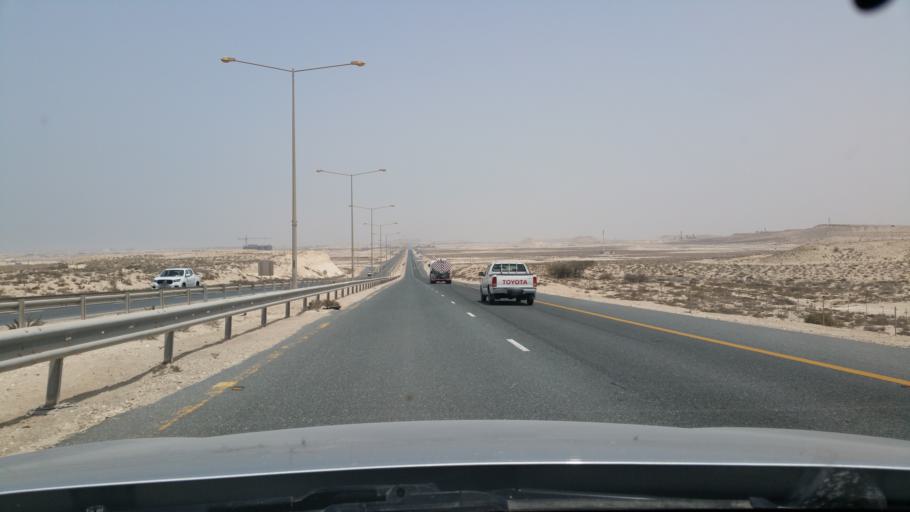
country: QA
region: Baladiyat ar Rayyan
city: Dukhan
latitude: 25.3605
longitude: 50.7795
